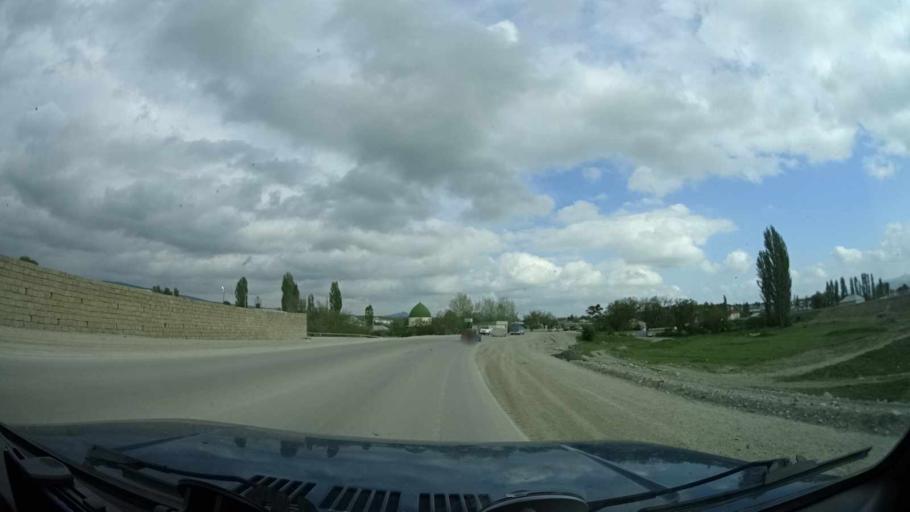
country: AZ
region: Samaxi
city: Shamakhi
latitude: 40.5951
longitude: 48.7011
